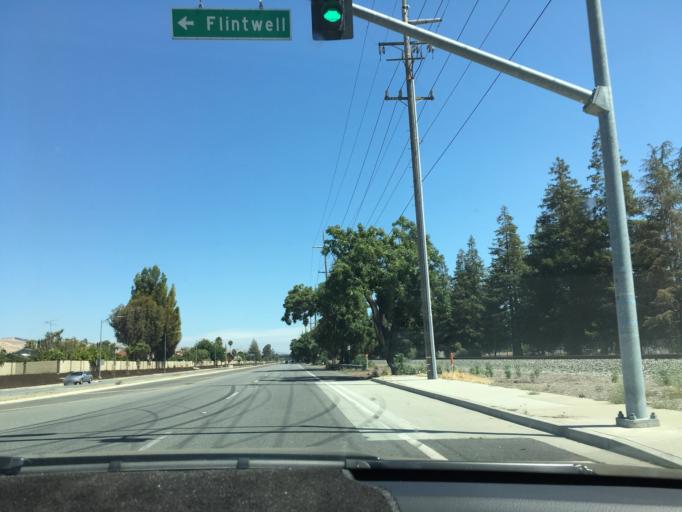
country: US
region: California
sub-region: Santa Clara County
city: Seven Trees
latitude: 37.2475
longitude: -121.7890
